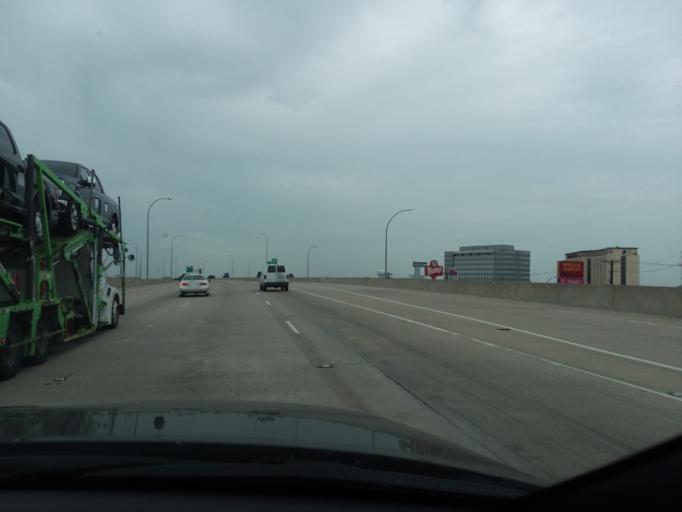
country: US
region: Texas
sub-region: Dallas County
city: Addison
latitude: 32.9255
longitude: -96.8383
